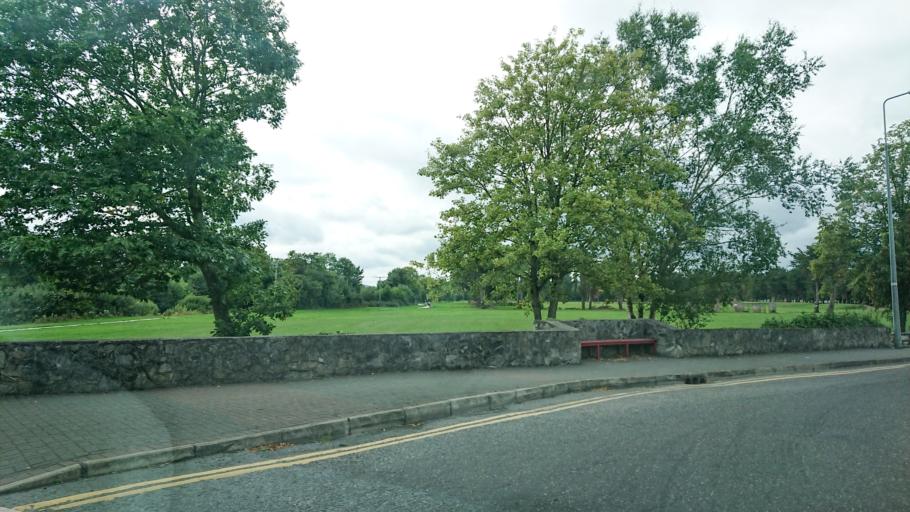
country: IE
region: Munster
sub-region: County Cork
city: Mallow
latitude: 52.1336
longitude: -8.6411
